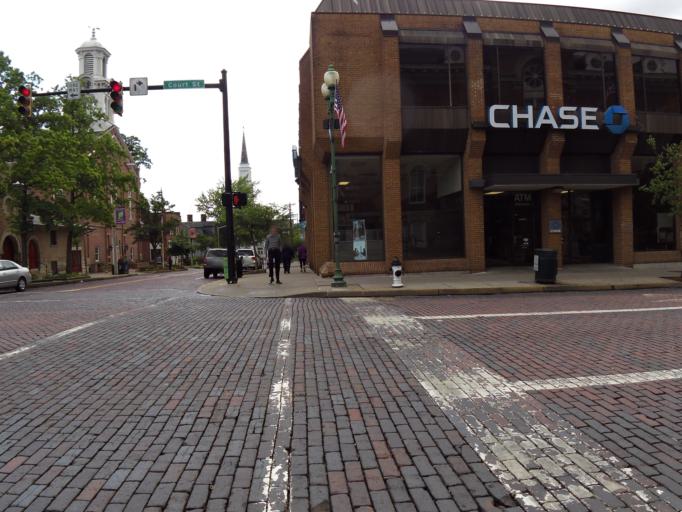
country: US
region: Ohio
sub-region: Athens County
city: Athens
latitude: 39.3292
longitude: -82.1013
